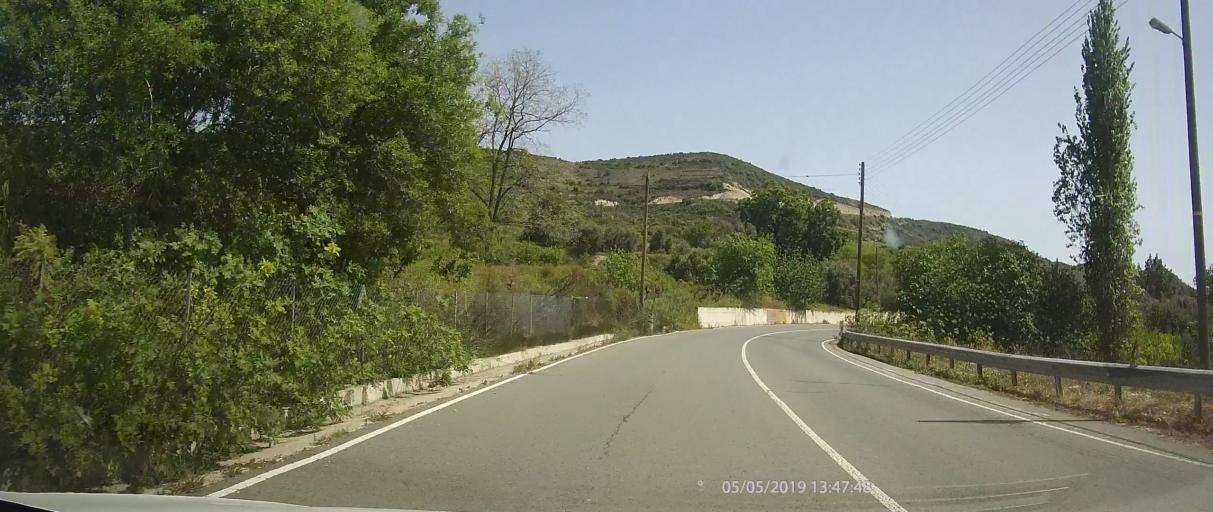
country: CY
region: Limassol
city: Pachna
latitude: 34.8627
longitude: 32.7562
